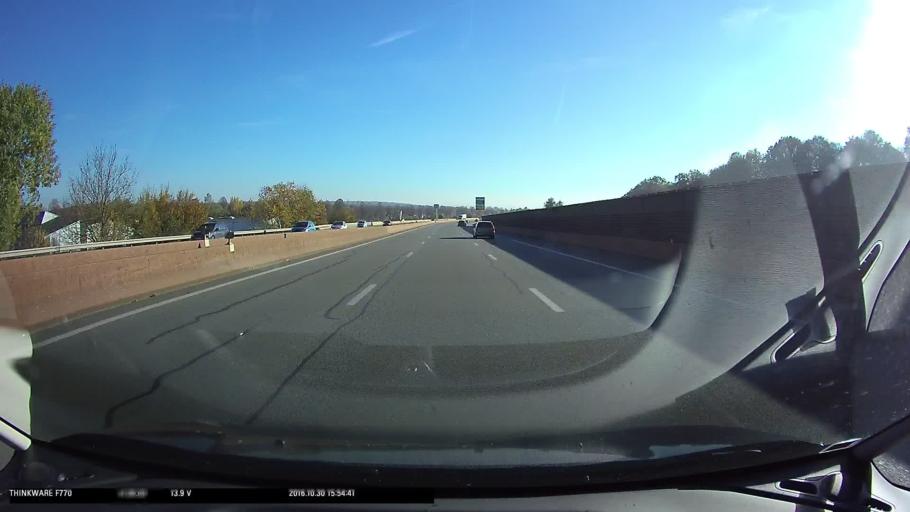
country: FR
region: Franche-Comte
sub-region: Territoire de Belfort
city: Andelnans
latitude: 47.5961
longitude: 6.8561
